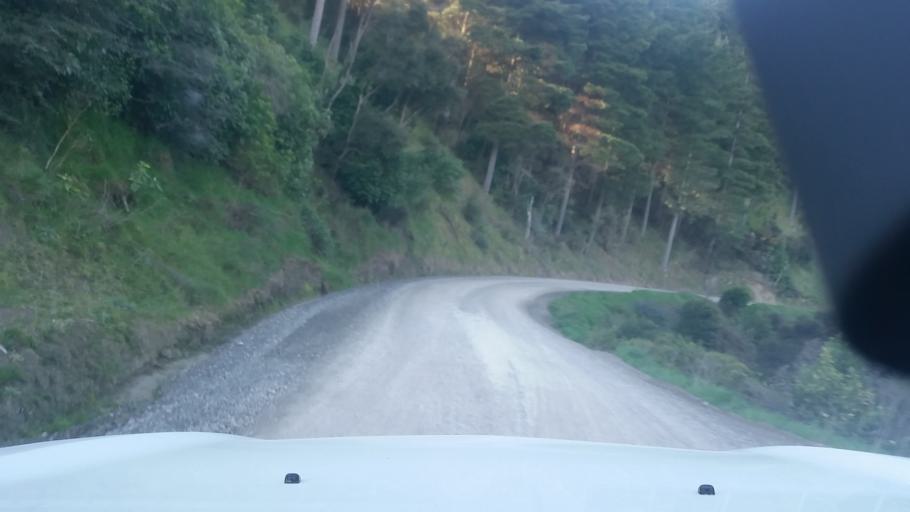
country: NZ
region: Wellington
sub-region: Masterton District
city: Castlepoint
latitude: -40.8573
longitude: 175.9439
